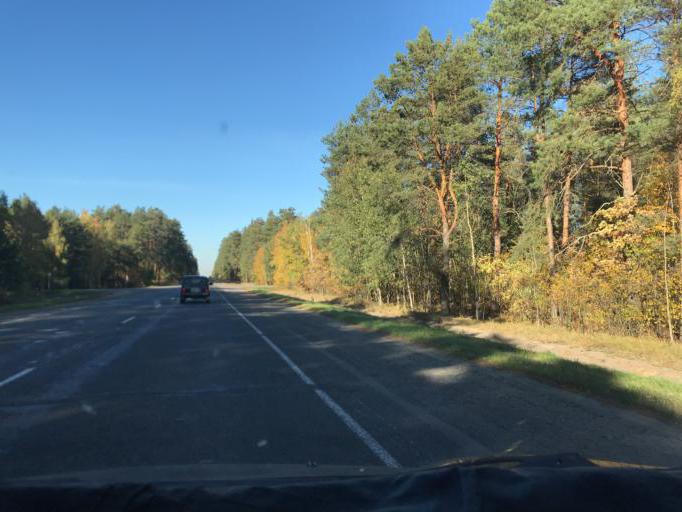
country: BY
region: Gomel
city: Kalinkavichy
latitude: 52.0549
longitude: 29.3611
